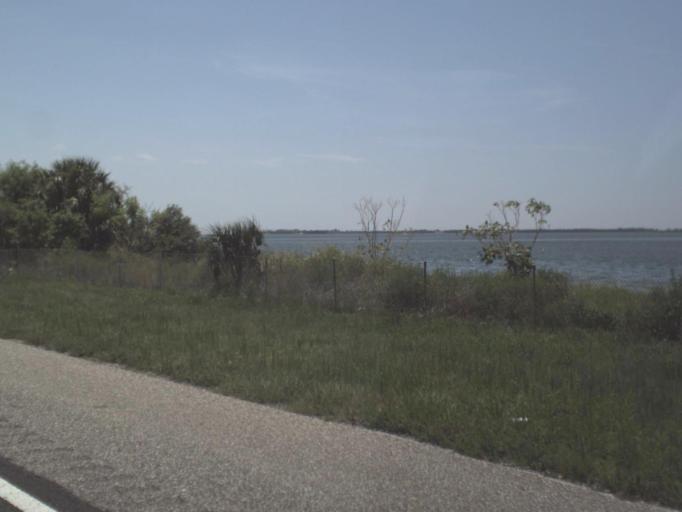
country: US
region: Florida
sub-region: Pinellas County
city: Tierra Verde
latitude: 27.6661
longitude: -82.6776
